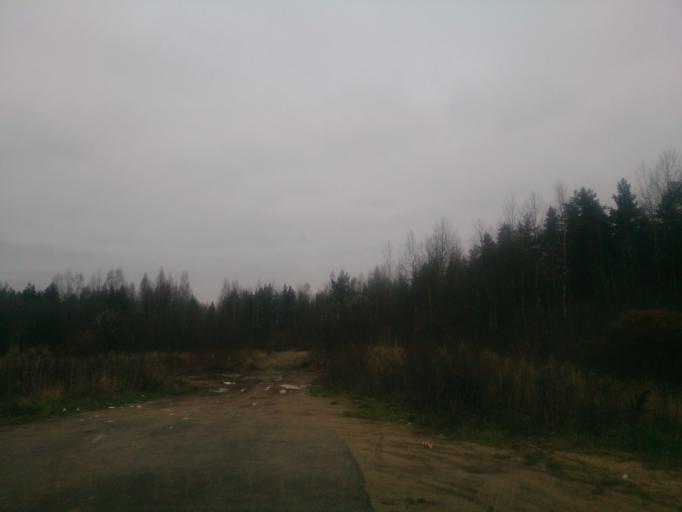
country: RU
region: Novgorod
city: Kresttsy
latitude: 58.3674
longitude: 32.1429
